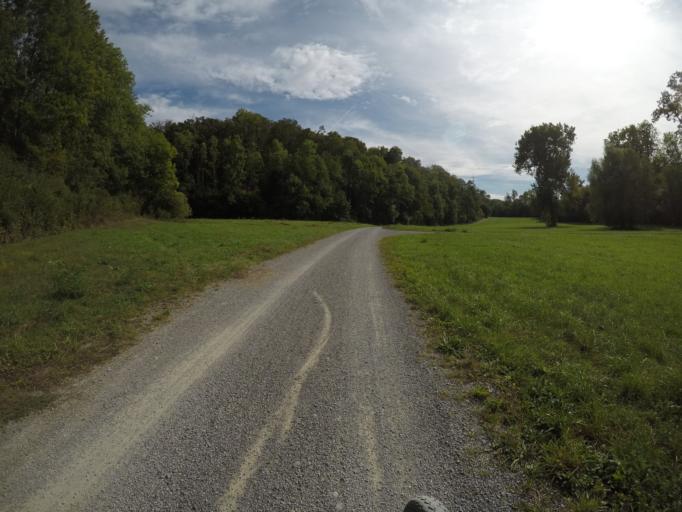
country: DE
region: Baden-Wuerttemberg
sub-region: Regierungsbezirk Stuttgart
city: Eberdingen
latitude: 48.9060
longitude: 8.9798
